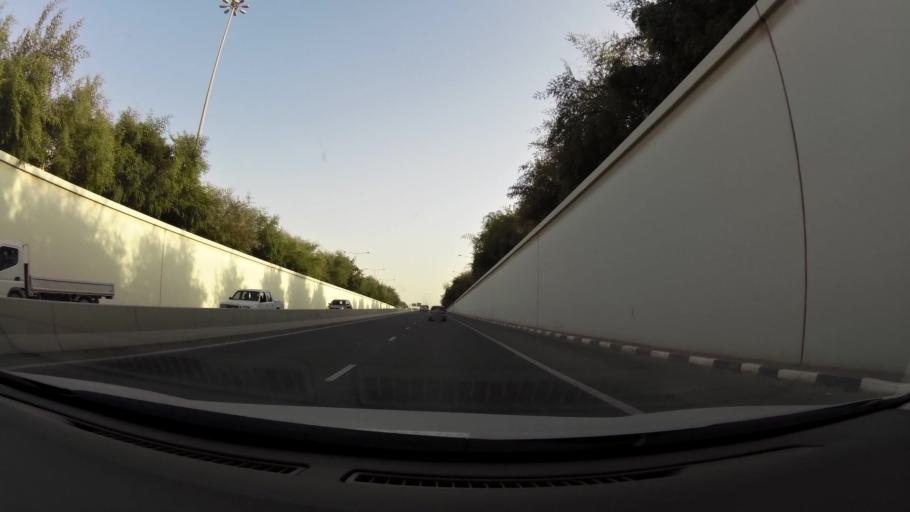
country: QA
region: Baladiyat ar Rayyan
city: Ar Rayyan
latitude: 25.3189
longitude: 51.4603
